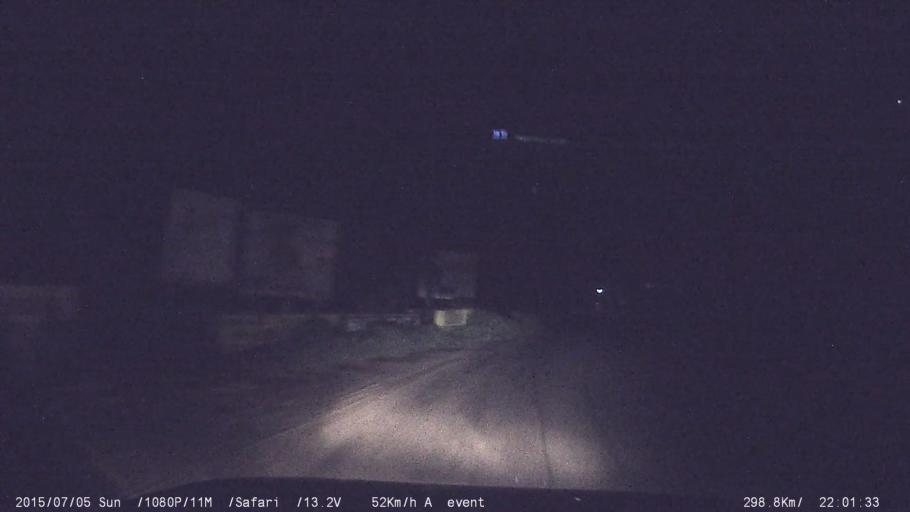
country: IN
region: Kerala
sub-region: Palakkad district
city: Mannarakkat
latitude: 10.9456
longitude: 76.5243
